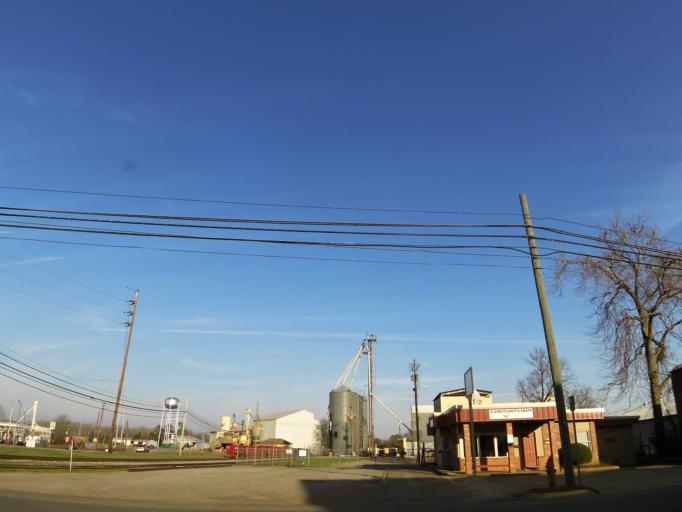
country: US
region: Georgia
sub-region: Webster County
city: Preston
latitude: 32.0337
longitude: -84.3927
